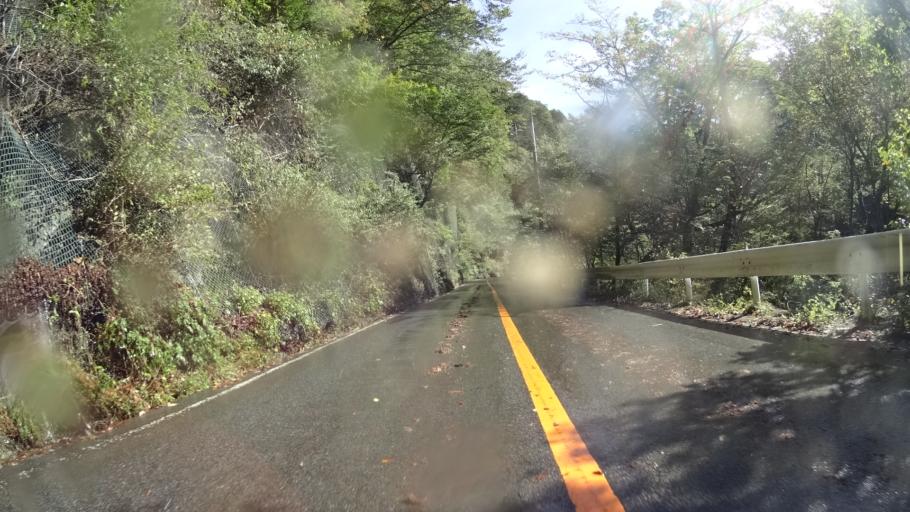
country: JP
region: Yamanashi
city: Enzan
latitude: 35.8056
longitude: 138.8474
